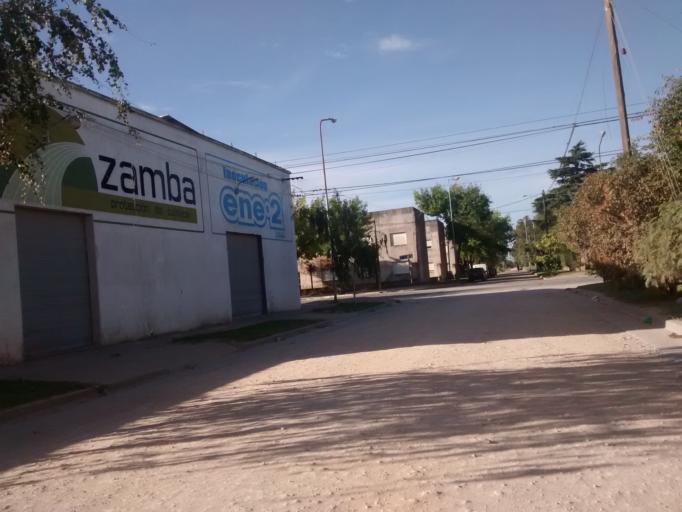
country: AR
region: Buenos Aires
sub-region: Partido de Loberia
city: Loberia
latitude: -38.1711
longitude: -58.7739
